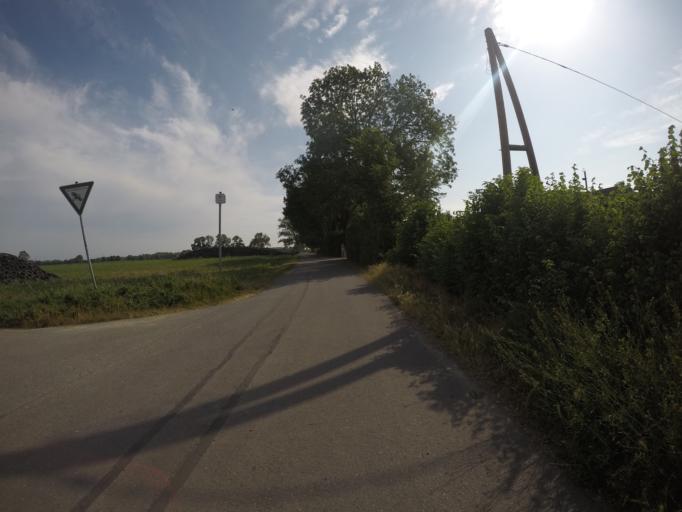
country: DE
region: North Rhine-Westphalia
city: Kalkar
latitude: 51.7473
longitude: 6.3371
